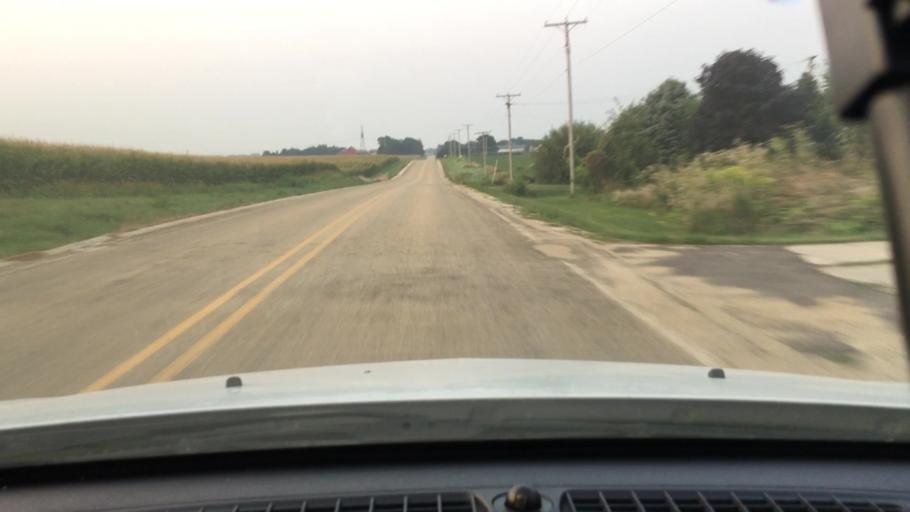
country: US
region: Illinois
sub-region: DeKalb County
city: Waterman
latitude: 41.8087
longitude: -88.7734
